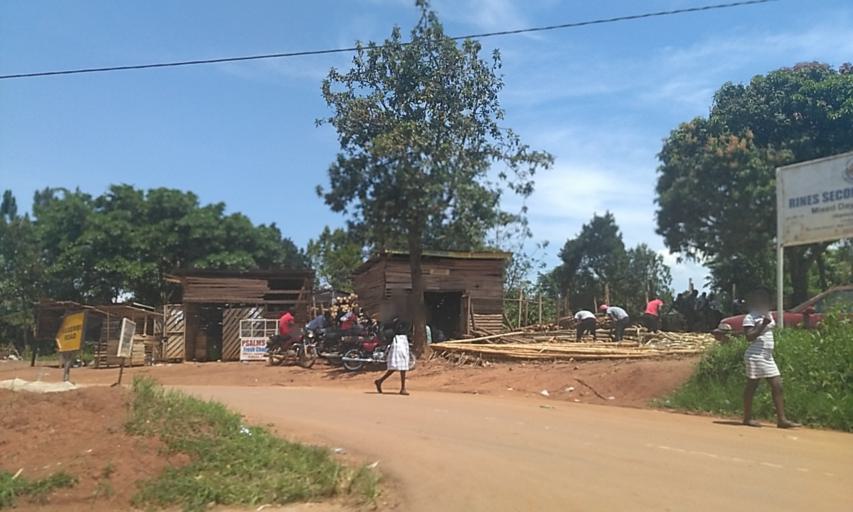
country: UG
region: Central Region
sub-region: Wakiso District
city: Wakiso
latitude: 0.4123
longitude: 32.4597
